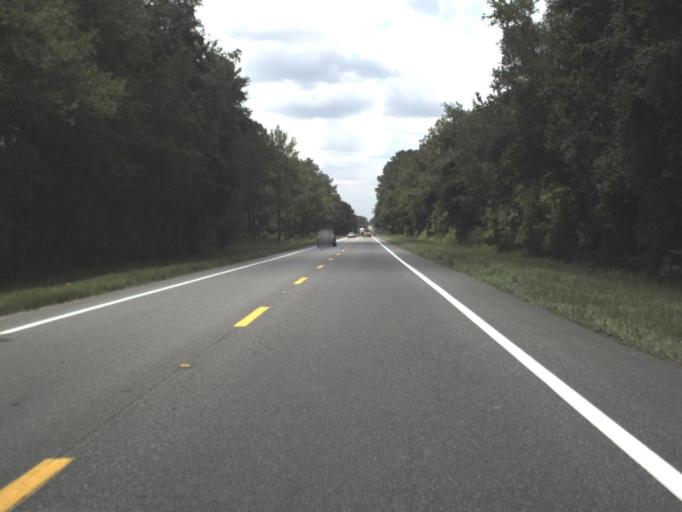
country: US
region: Florida
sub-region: Columbia County
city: Five Points
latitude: 30.2348
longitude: -82.6673
